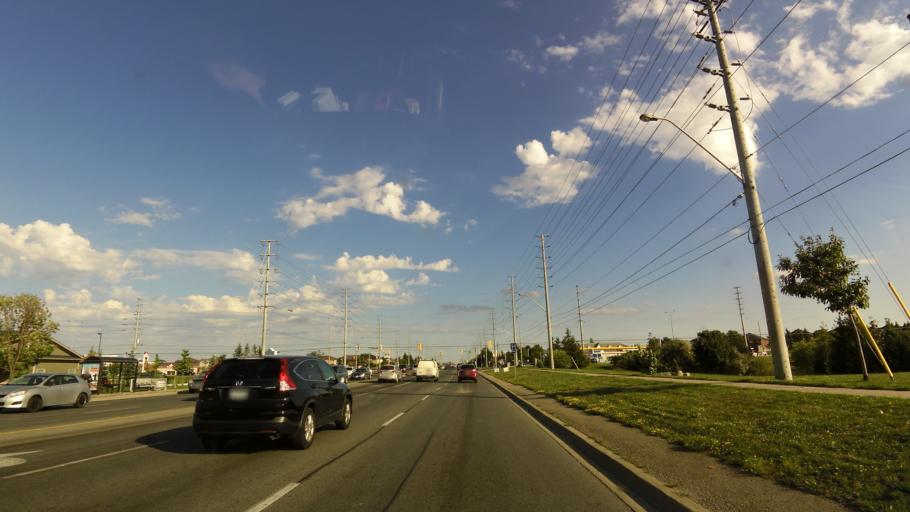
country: CA
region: Ontario
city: Brampton
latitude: 43.6871
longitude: -79.8098
